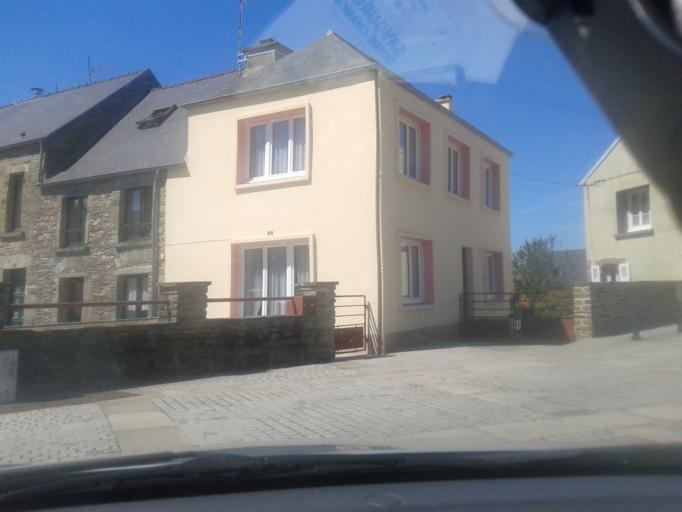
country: FR
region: Lower Normandy
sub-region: Departement de la Manche
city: Octeville
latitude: 49.6254
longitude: -1.6433
